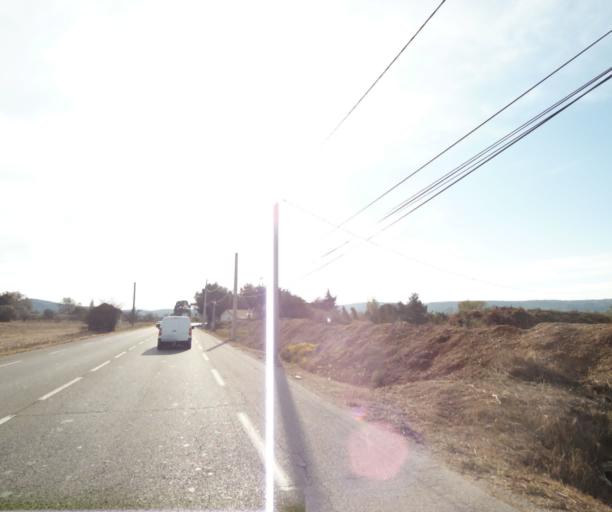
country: FR
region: Provence-Alpes-Cote d'Azur
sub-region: Departement des Bouches-du-Rhone
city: Chateauneuf-les-Martigues
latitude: 43.3892
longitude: 5.1934
